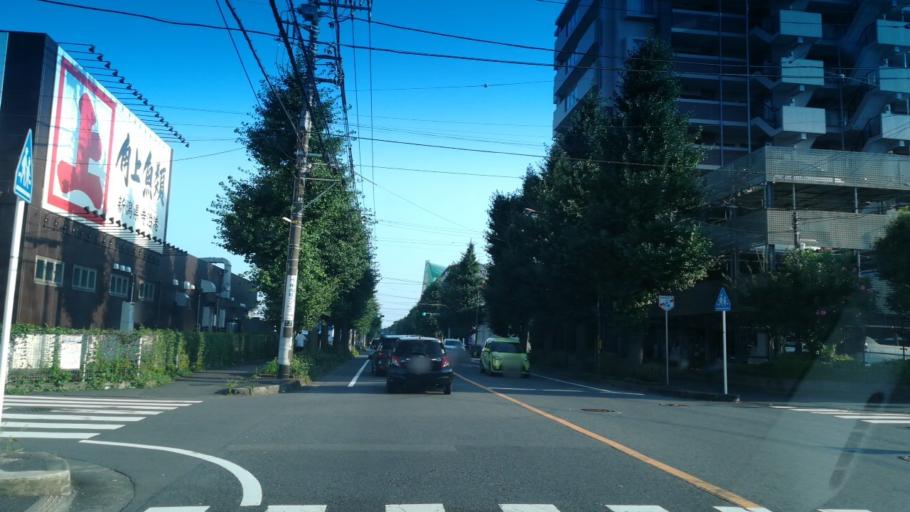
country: JP
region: Tokyo
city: Hachioji
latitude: 35.5801
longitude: 139.3549
